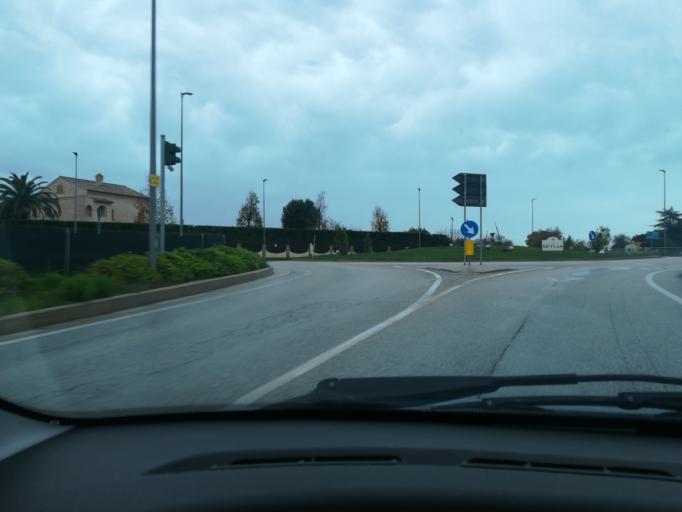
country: IT
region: The Marches
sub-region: Provincia di Macerata
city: Borgo Stazione
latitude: 43.2902
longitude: 13.6541
